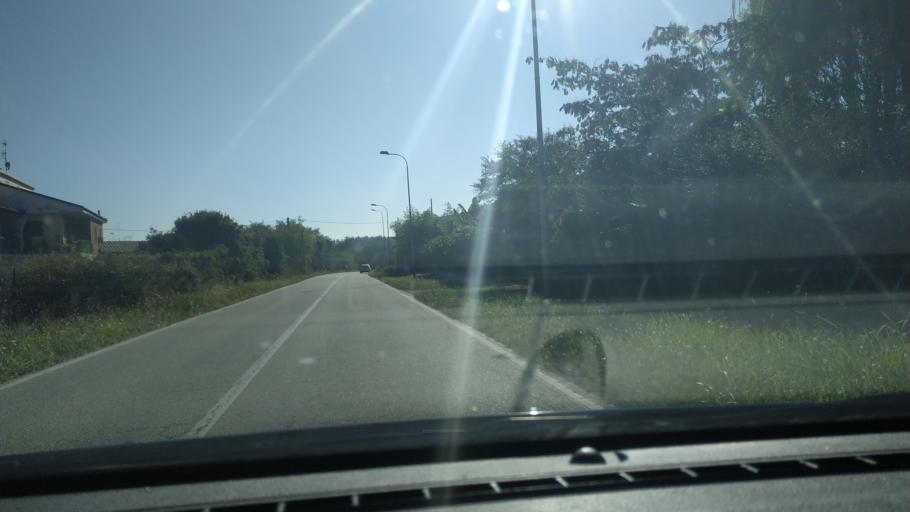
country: IT
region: Piedmont
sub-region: Provincia di Torino
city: Verolengo
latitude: 45.1950
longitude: 7.9467
